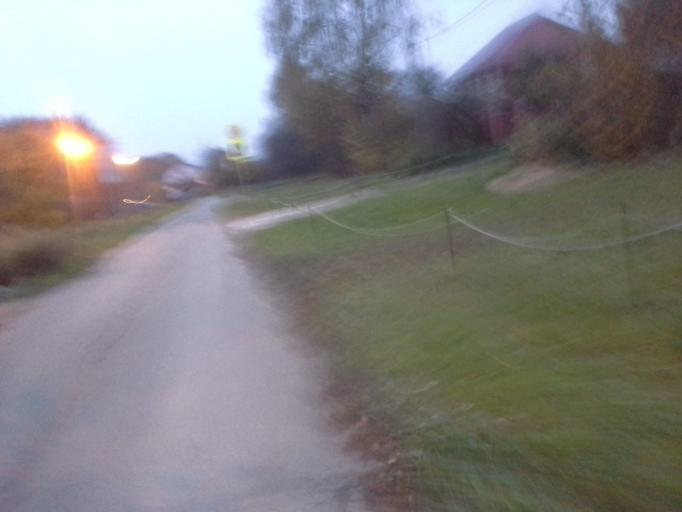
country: RU
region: Moskovskaya
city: Nazar'yevo
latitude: 55.6899
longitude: 37.0307
